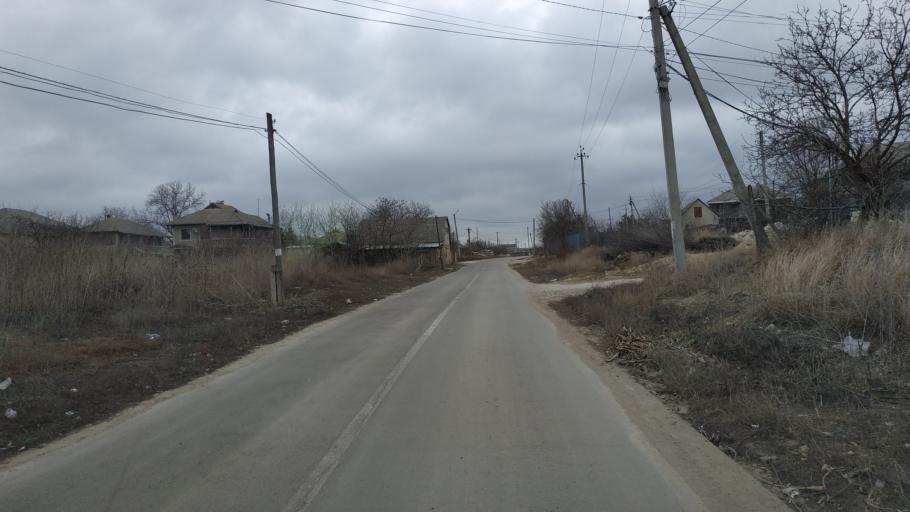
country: MD
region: Laloveni
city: Ialoveni
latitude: 46.9366
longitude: 28.7933
